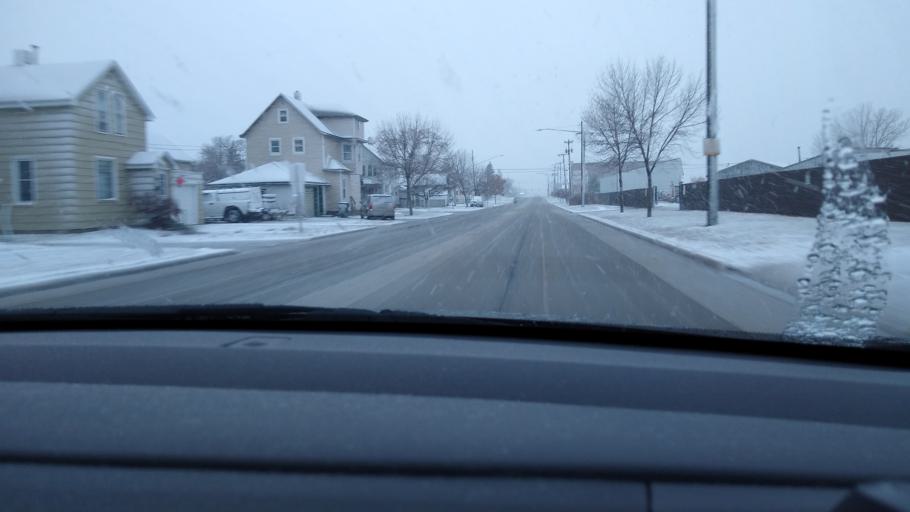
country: US
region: Michigan
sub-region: Delta County
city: Escanaba
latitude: 45.7494
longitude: -87.0662
